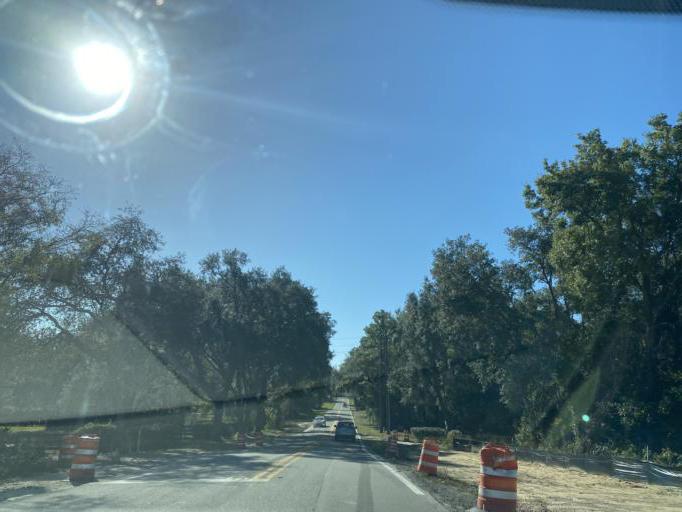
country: US
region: Florida
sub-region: Orange County
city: Tangerine
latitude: 28.7994
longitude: -81.5928
